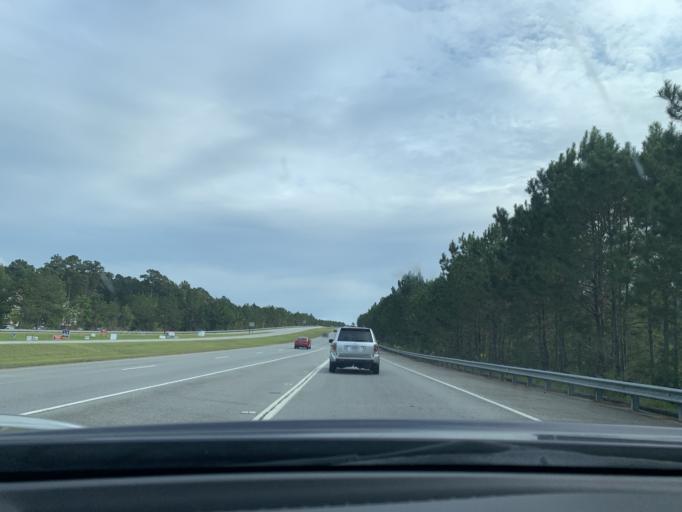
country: US
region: Georgia
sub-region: Chatham County
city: Pooler
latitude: 32.1159
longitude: -81.2690
